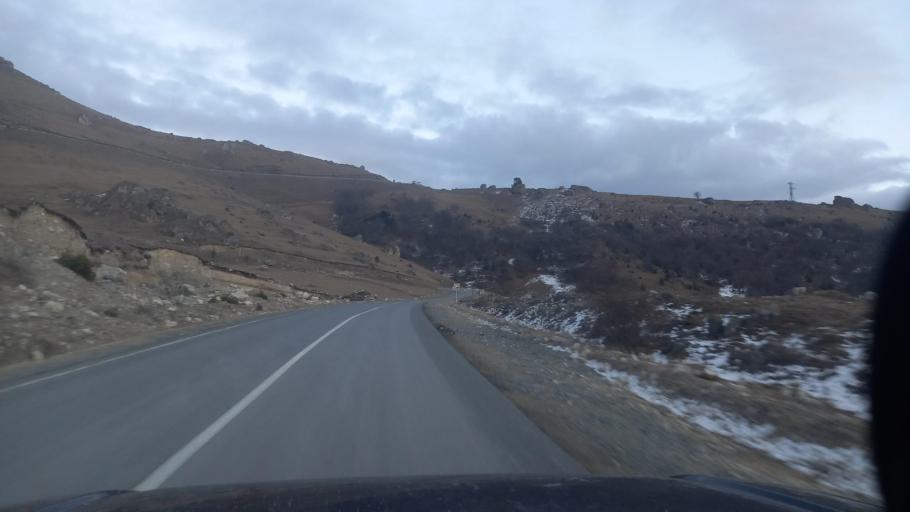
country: RU
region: Ingushetiya
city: Dzhayrakh
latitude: 42.8212
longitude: 44.8239
